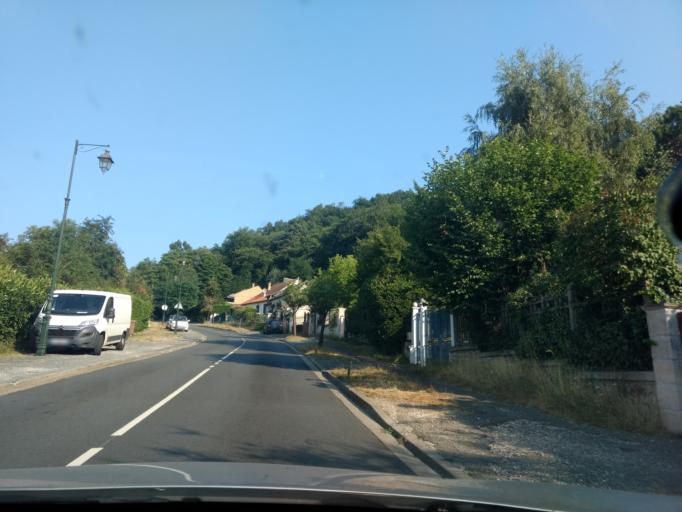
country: FR
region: Ile-de-France
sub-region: Departement de l'Essonne
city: Bievres
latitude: 48.7573
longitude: 2.2104
